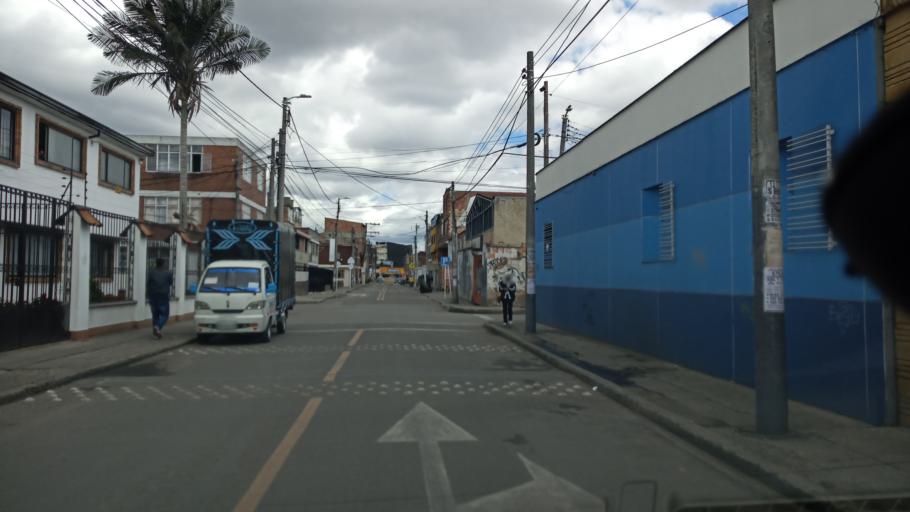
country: CO
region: Cundinamarca
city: Funza
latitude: 4.6723
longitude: -74.1435
